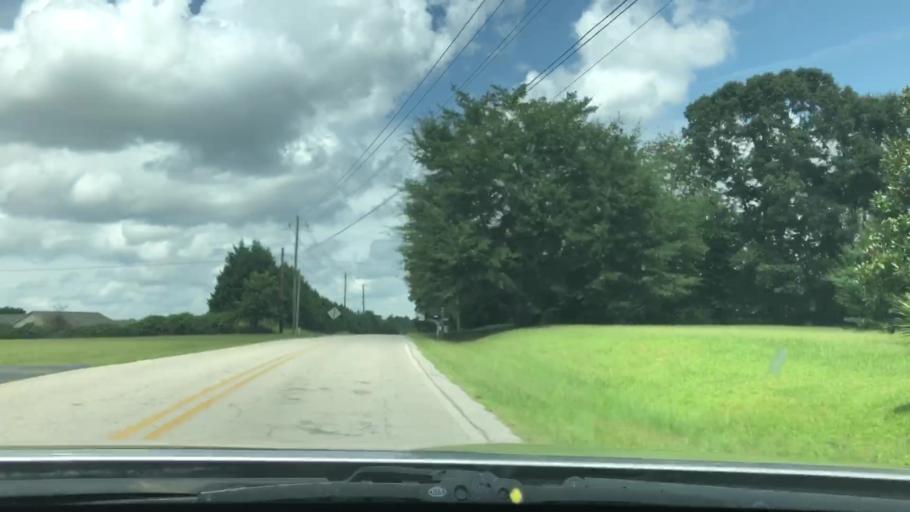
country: US
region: Georgia
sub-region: Henry County
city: Locust Grove
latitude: 33.3860
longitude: -84.1227
